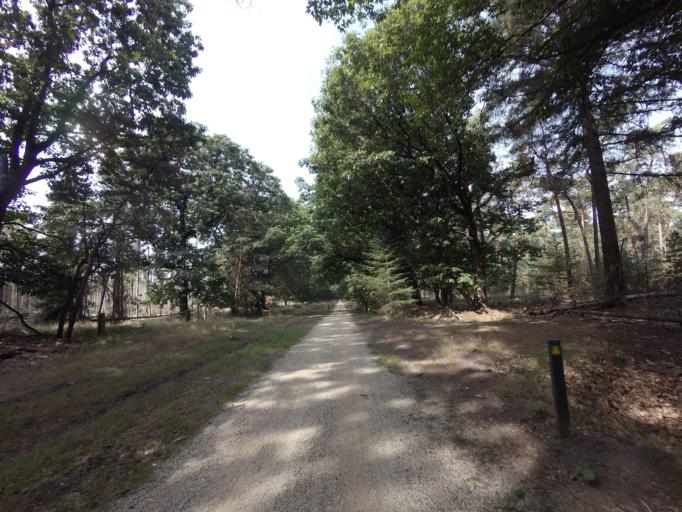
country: NL
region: North Brabant
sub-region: Gemeente Mill en Sint Hubert
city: Wilbertoord
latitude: 51.5397
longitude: 5.7785
